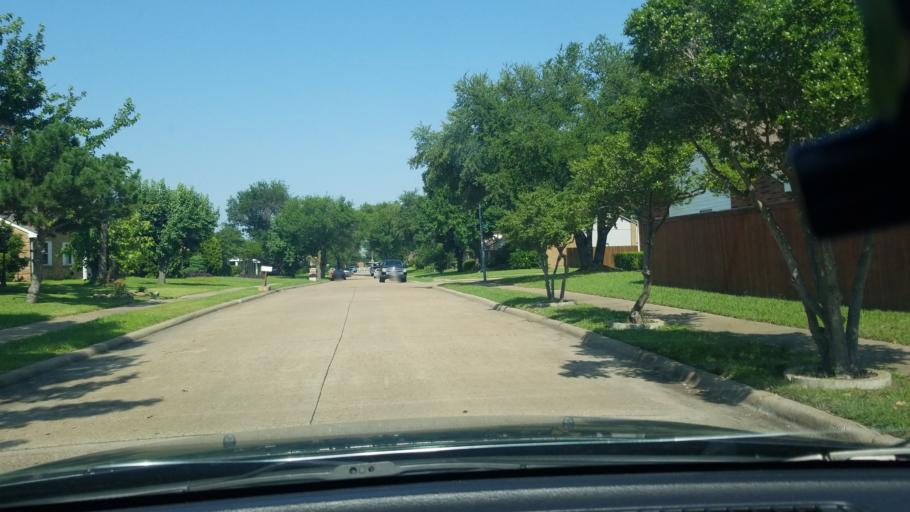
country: US
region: Texas
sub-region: Dallas County
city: Mesquite
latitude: 32.8203
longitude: -96.6240
